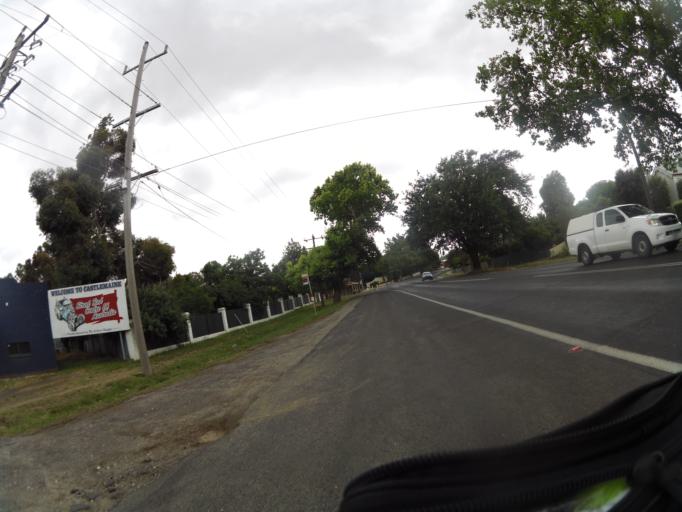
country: AU
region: Victoria
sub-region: Mount Alexander
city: Castlemaine
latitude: -37.0708
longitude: 144.2110
